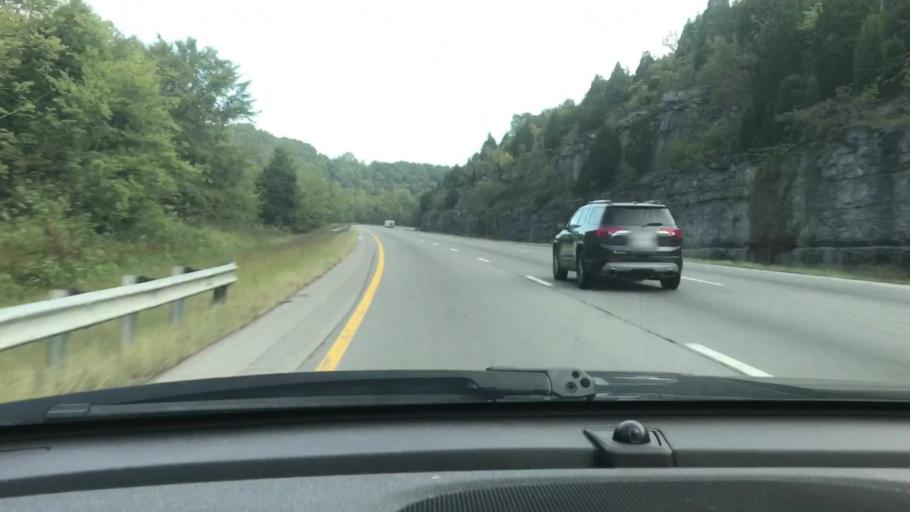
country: US
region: Tennessee
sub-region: Sumner County
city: Millersville
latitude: 36.4068
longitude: -86.7199
